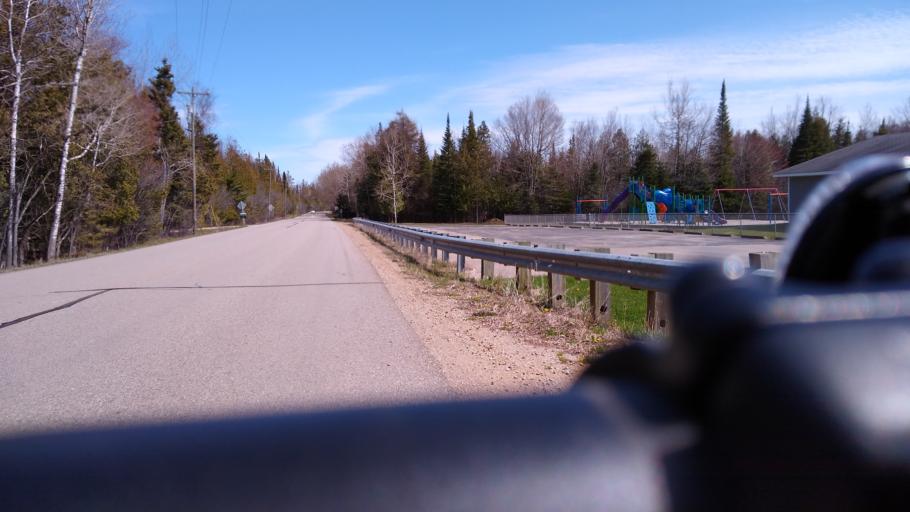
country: US
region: Michigan
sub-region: Delta County
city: Escanaba
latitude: 45.6862
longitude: -87.1514
